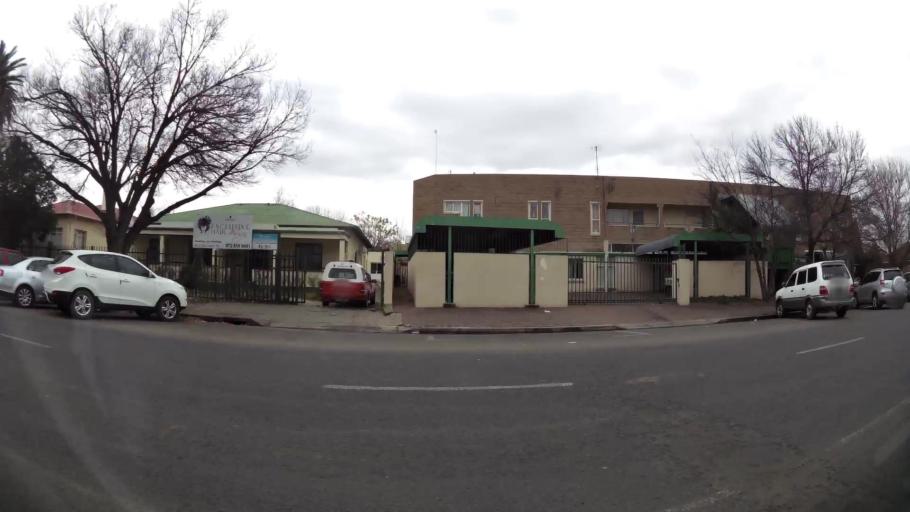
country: ZA
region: Orange Free State
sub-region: Fezile Dabi District Municipality
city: Kroonstad
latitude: -27.6617
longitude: 27.2390
